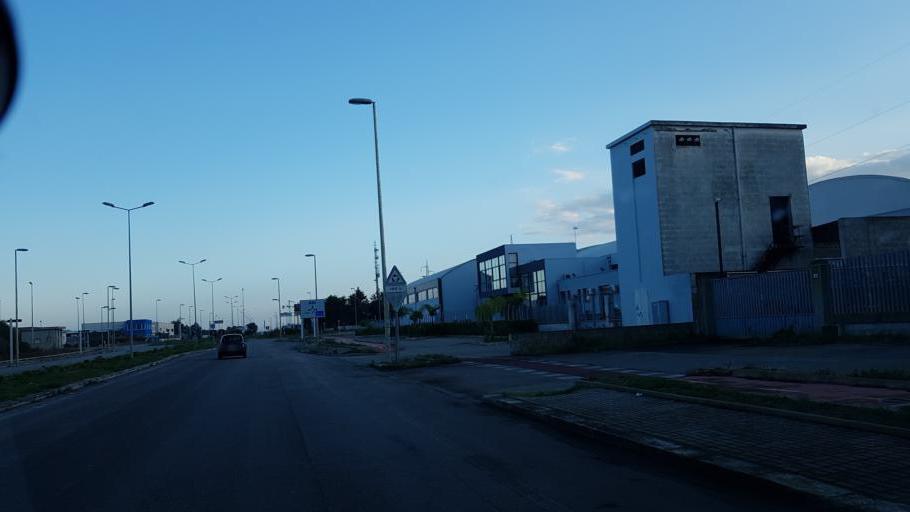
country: IT
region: Apulia
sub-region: Provincia di Lecce
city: Surbo
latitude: 40.3809
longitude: 18.1239
